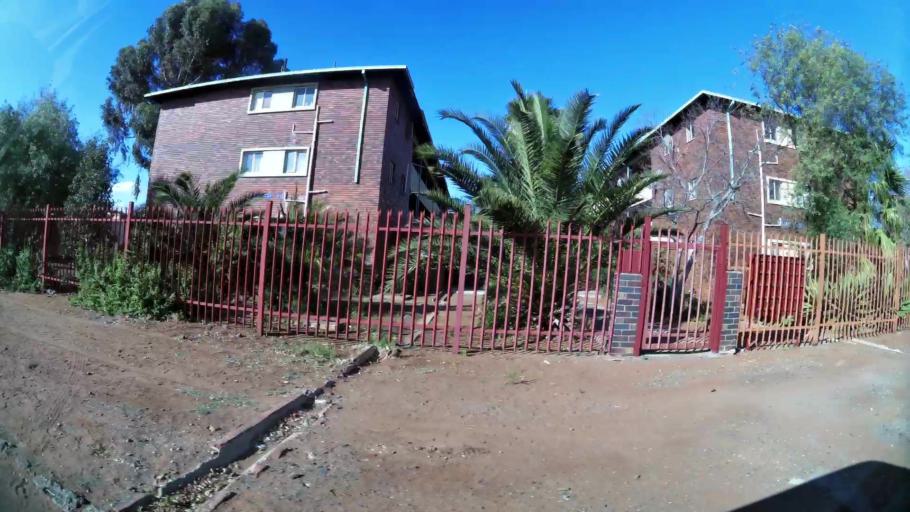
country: ZA
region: Northern Cape
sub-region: Frances Baard District Municipality
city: Kimberley
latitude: -28.7472
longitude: 24.7617
